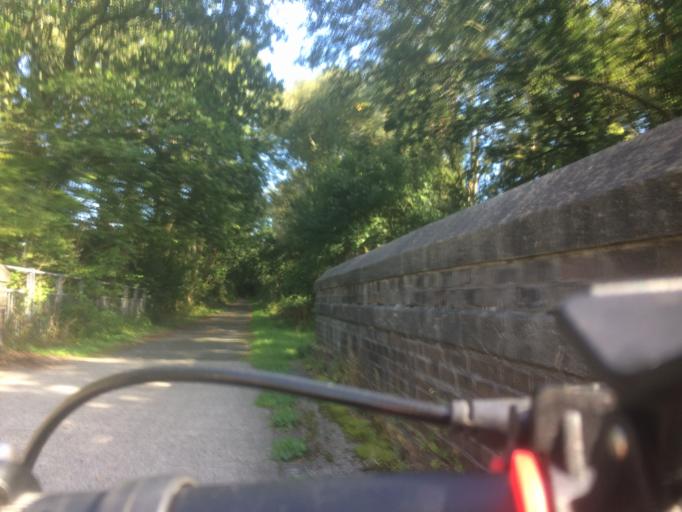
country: GB
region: England
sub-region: Devon
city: Horrabridge
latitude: 50.5109
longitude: -4.1111
